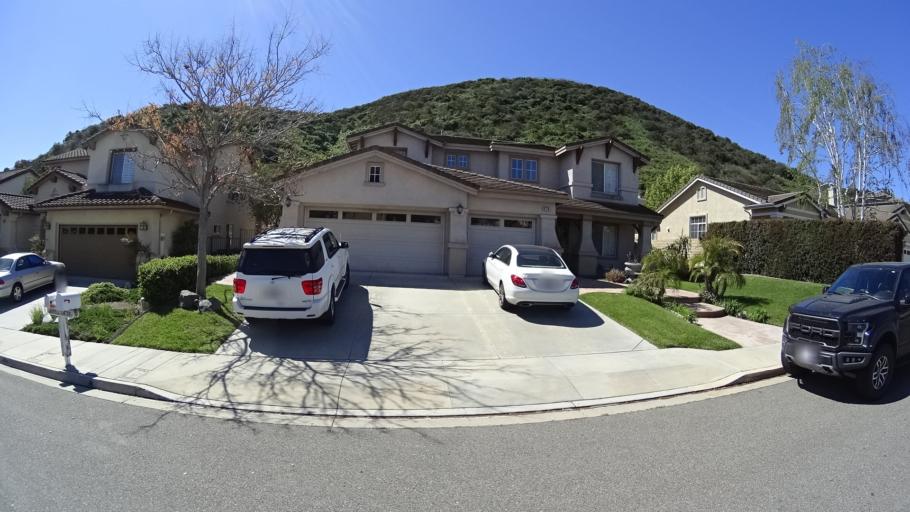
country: US
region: California
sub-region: Ventura County
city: Casa Conejo
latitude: 34.1648
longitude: -118.9757
